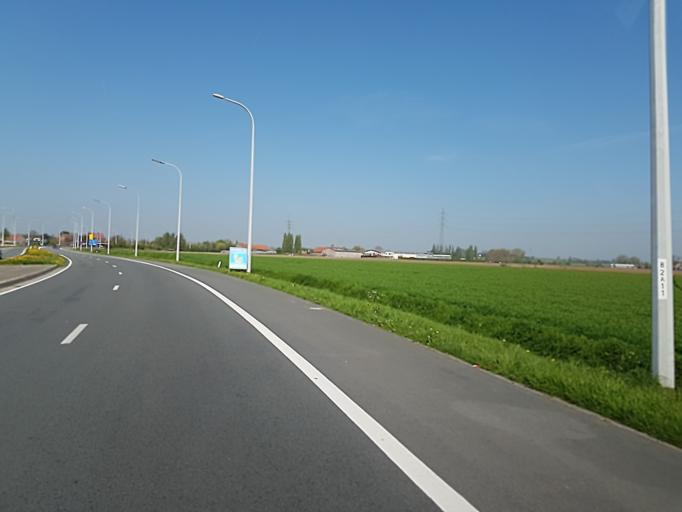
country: BE
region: Flanders
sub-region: Provincie West-Vlaanderen
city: Menen
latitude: 50.8180
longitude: 3.1249
